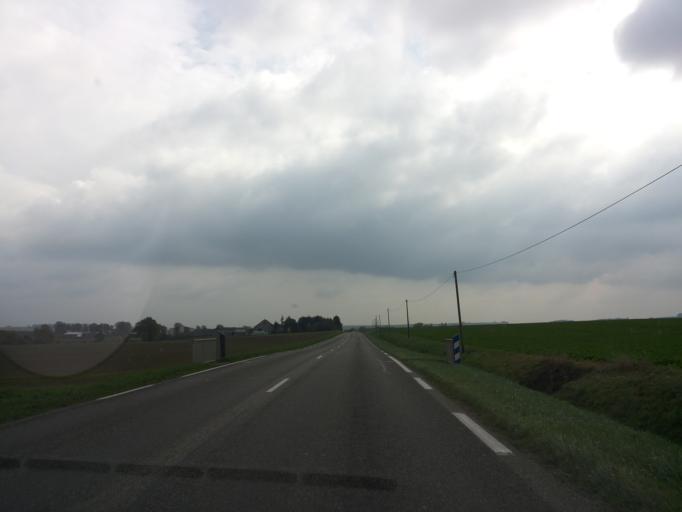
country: FR
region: Lorraine
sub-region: Departement de la Moselle
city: Vic-sur-Seille
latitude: 48.7906
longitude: 6.5630
